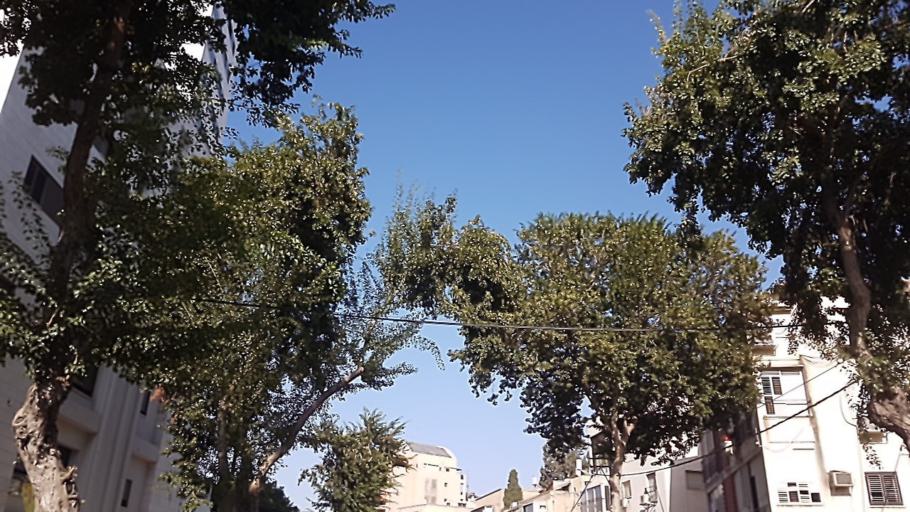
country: IL
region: Tel Aviv
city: Ramat Gan
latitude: 32.0804
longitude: 34.8178
